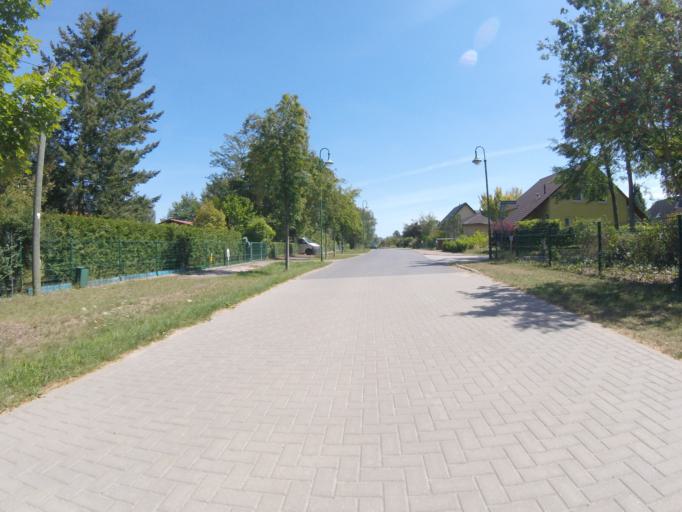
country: DE
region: Brandenburg
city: Bestensee
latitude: 52.2666
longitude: 13.6237
